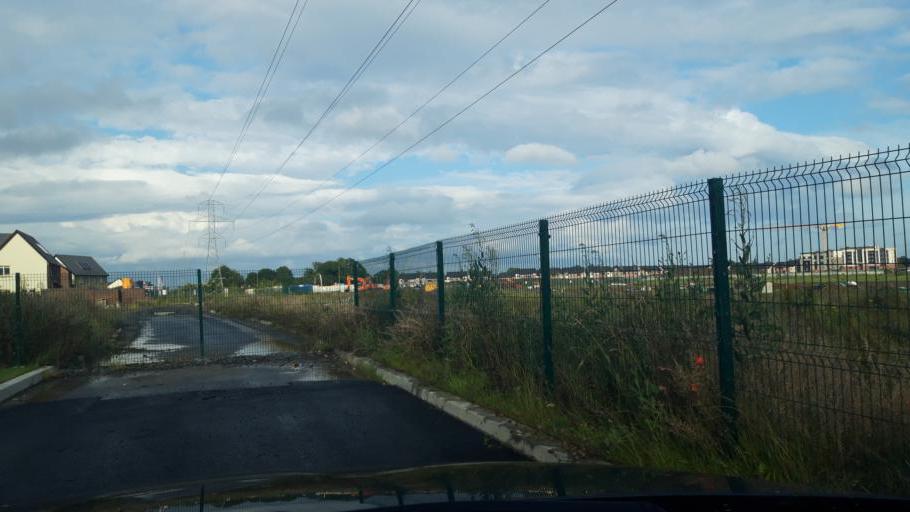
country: IE
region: Leinster
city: Hartstown
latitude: 53.3893
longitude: -6.4433
